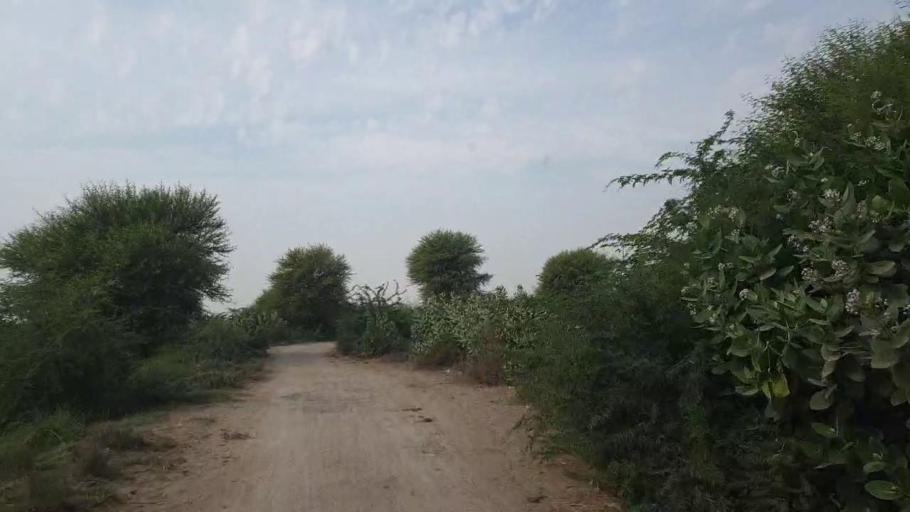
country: PK
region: Sindh
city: Rajo Khanani
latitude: 24.9725
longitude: 68.9957
